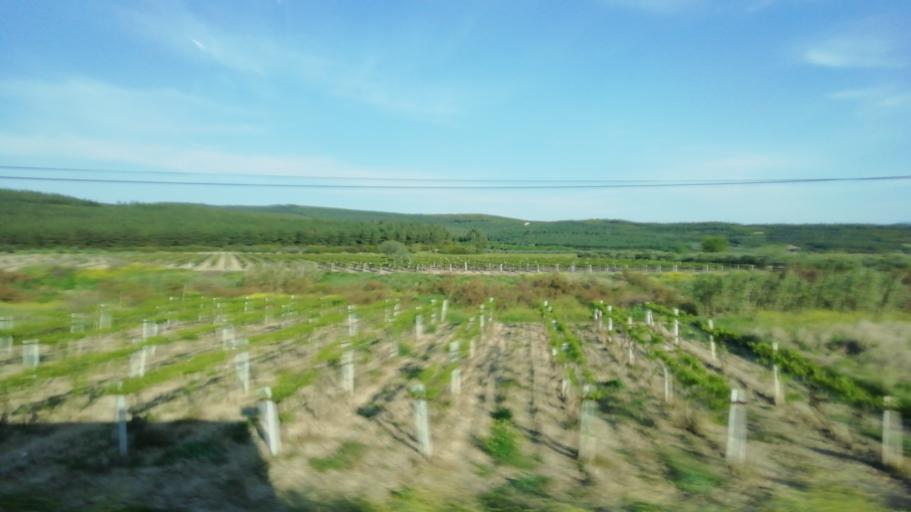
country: TR
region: Manisa
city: Halitpasa
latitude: 38.7859
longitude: 27.6705
